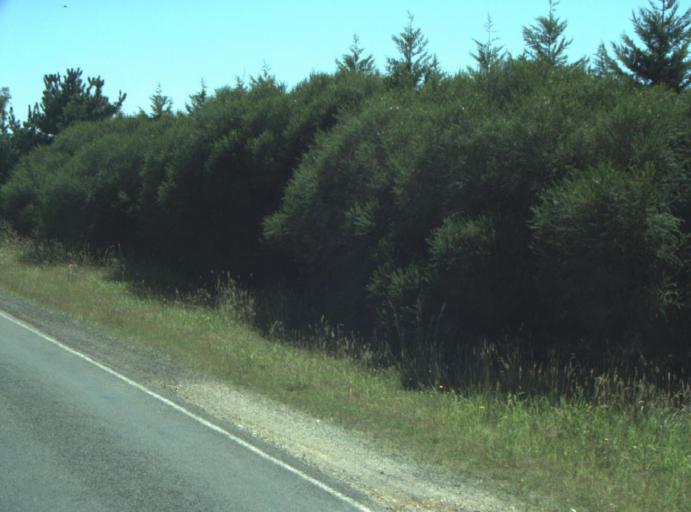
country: AU
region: Victoria
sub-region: Greater Geelong
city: Breakwater
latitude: -38.2086
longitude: 144.3589
